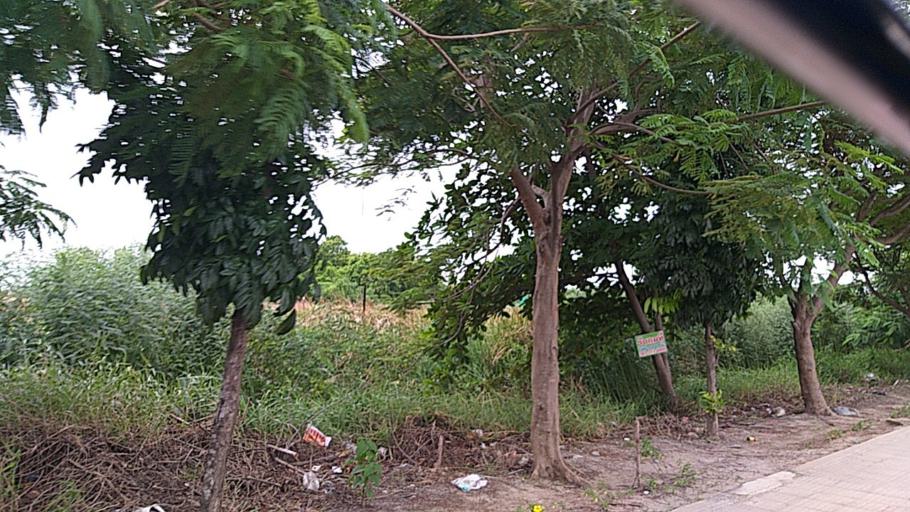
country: TH
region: Bangkok
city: Bang Na
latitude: 13.6626
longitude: 100.6818
